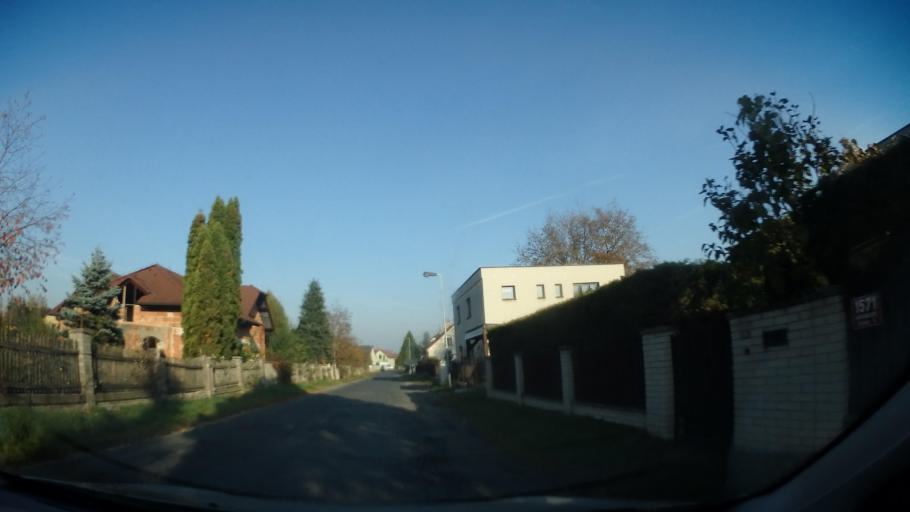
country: CZ
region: Central Bohemia
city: Sestajovice
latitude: 50.0710
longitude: 14.6754
